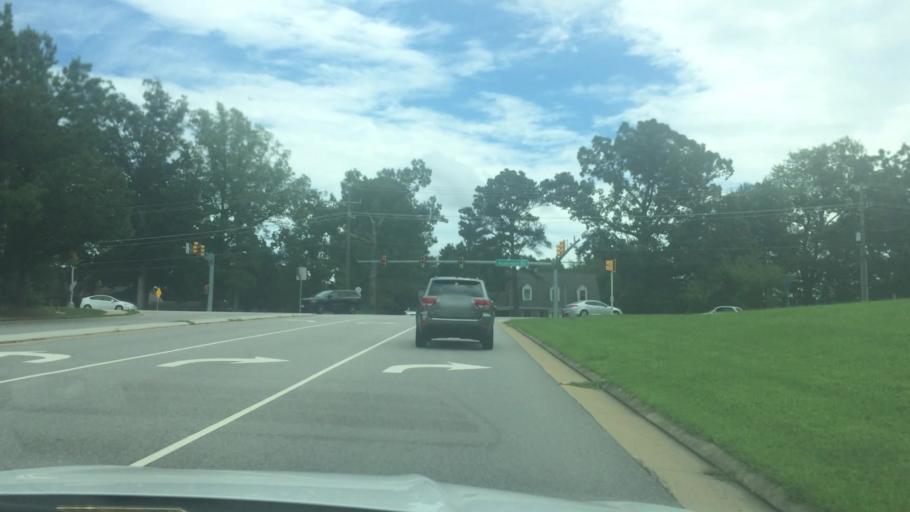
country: US
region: Virginia
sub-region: James City County
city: Williamsburg
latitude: 37.2690
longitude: -76.7585
